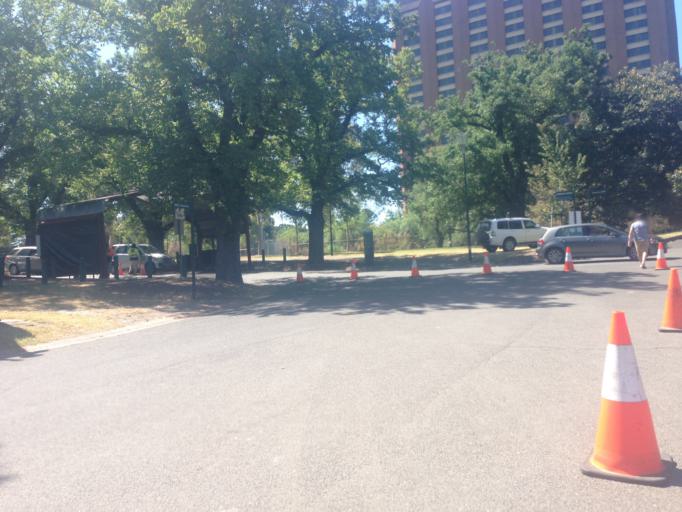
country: AU
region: Victoria
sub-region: Melbourne
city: East Melbourne
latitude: -37.8172
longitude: 144.9833
